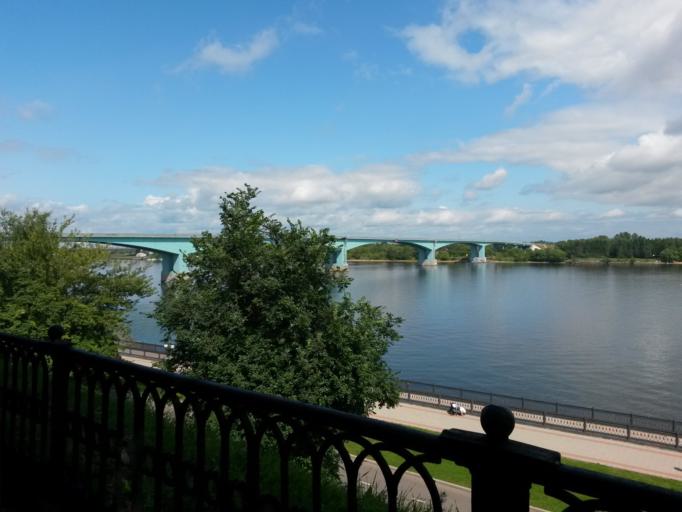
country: RU
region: Jaroslavl
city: Yaroslavl
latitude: 57.6372
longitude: 39.8901
